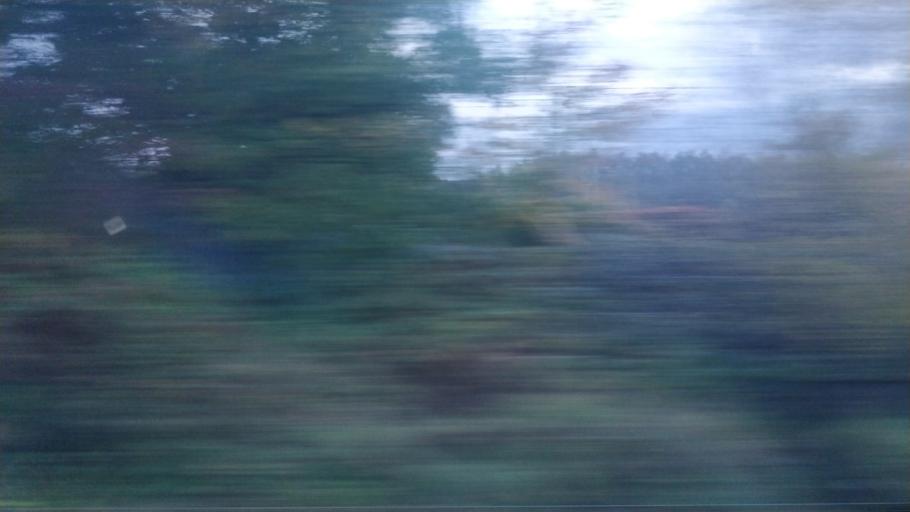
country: GB
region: England
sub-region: Lancashire
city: Parbold
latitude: 53.5884
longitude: -2.7611
